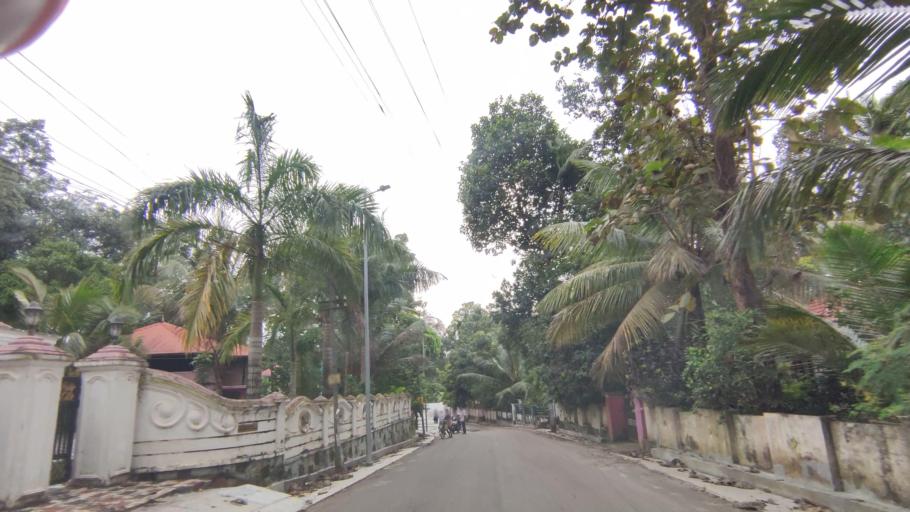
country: IN
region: Kerala
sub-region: Kottayam
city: Kottayam
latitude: 9.6611
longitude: 76.5110
